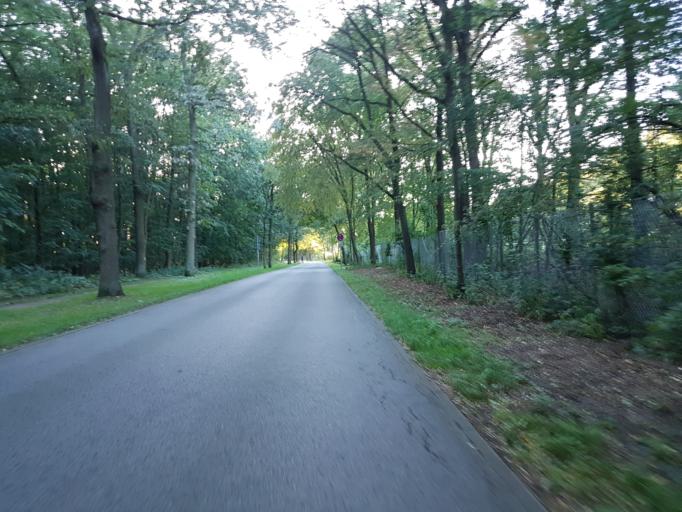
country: DE
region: Lower Saxony
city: Langenhagen
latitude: 52.4443
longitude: 9.7608
